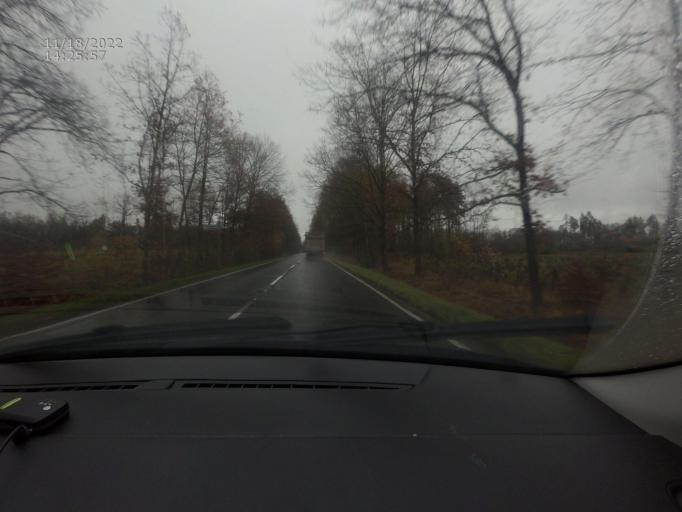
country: CZ
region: Jihocesky
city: Cimelice
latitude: 49.4328
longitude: 14.1633
